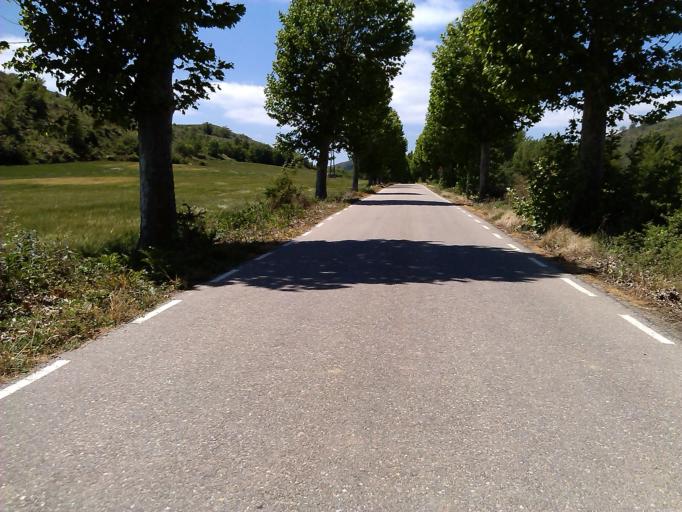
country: ES
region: Castille and Leon
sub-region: Provincia de Burgos
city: Alcocero de Mola
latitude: 42.4531
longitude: -3.3390
